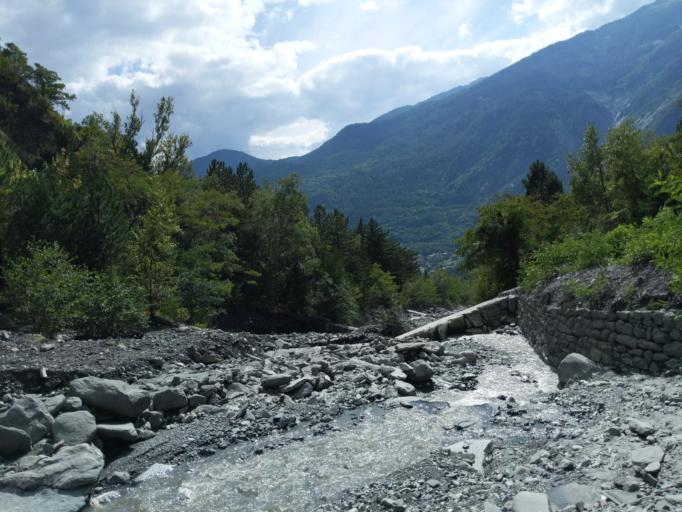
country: FR
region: Rhone-Alpes
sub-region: Departement de la Savoie
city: Villargondran
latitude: 45.2609
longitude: 6.4027
